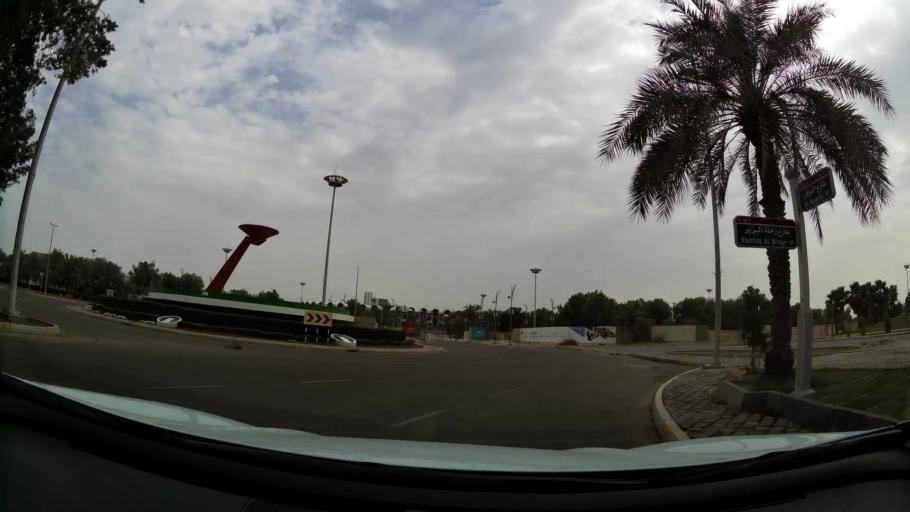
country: AE
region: Abu Dhabi
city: Abu Dhabi
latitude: 24.4177
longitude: 54.4483
